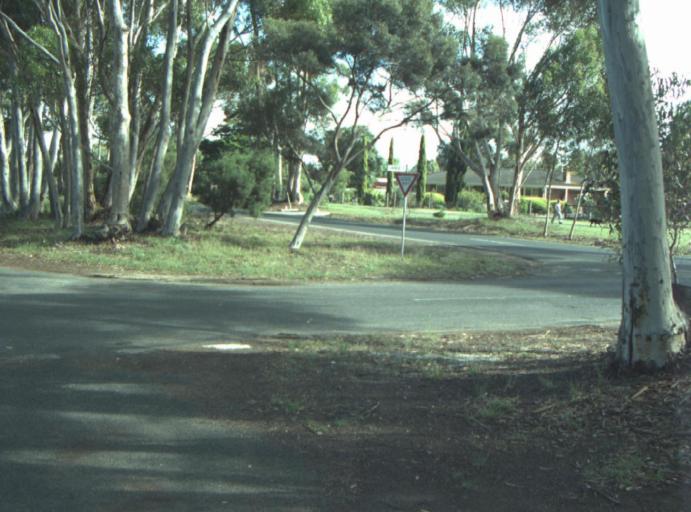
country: AU
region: Victoria
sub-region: Greater Geelong
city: Lara
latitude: -38.0213
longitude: 144.3944
